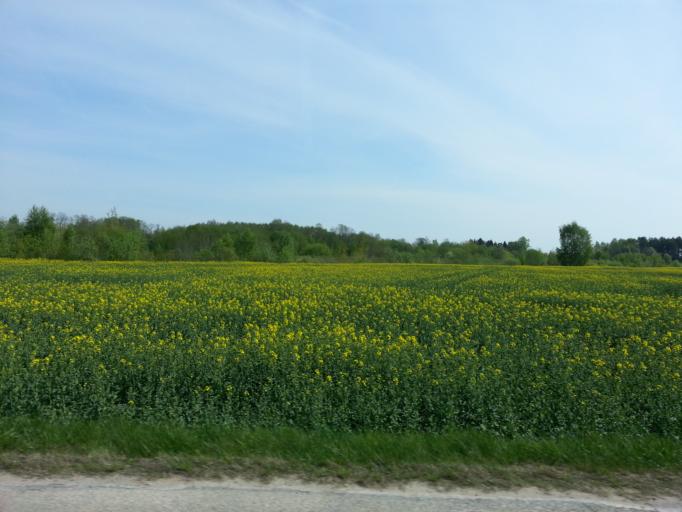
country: LT
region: Panevezys
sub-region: Panevezys City
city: Panevezys
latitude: 55.8063
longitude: 24.2724
